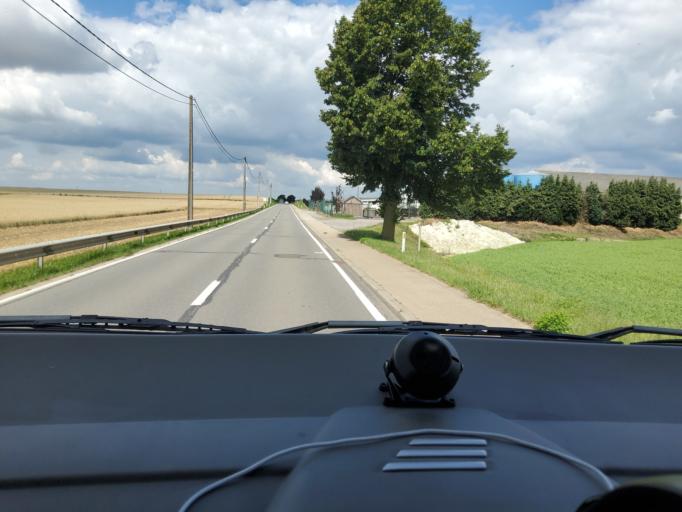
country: BE
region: Wallonia
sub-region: Province du Brabant Wallon
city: Genappe
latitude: 50.5736
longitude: 4.4468
